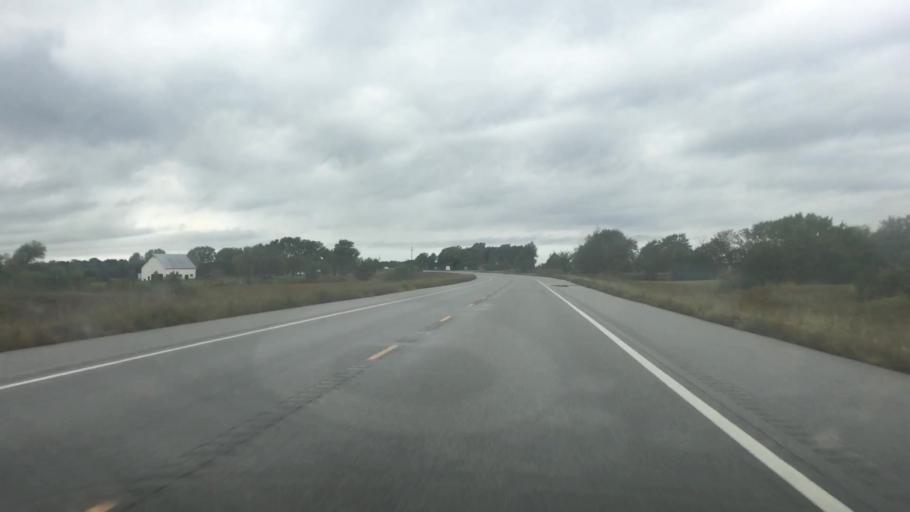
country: US
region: Kansas
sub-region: Miami County
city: Osawatomie
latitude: 38.4427
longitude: -94.9927
